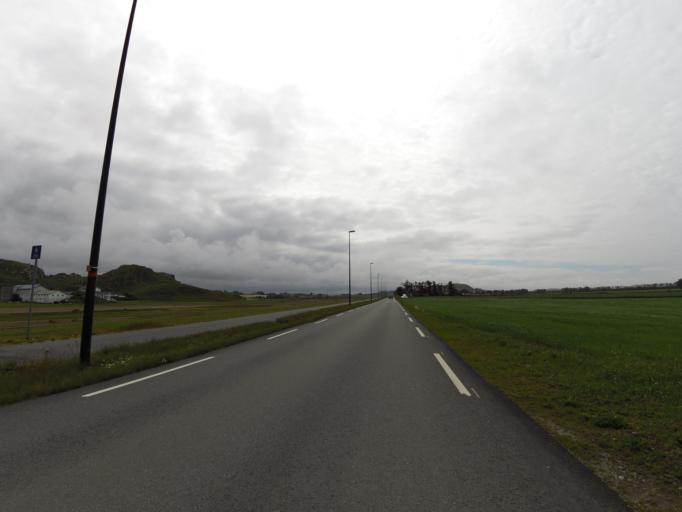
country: NO
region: Rogaland
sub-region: Klepp
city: Kleppe
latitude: 58.8425
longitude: 5.5681
